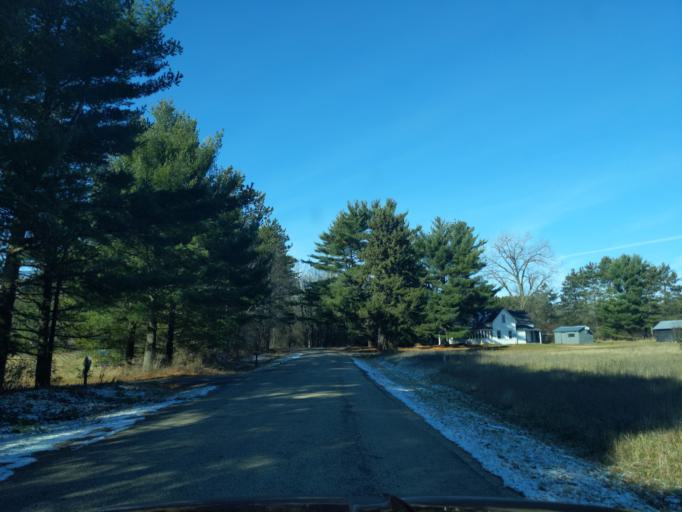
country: US
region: Wisconsin
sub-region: Waushara County
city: Silver Lake
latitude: 44.1122
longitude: -89.1718
